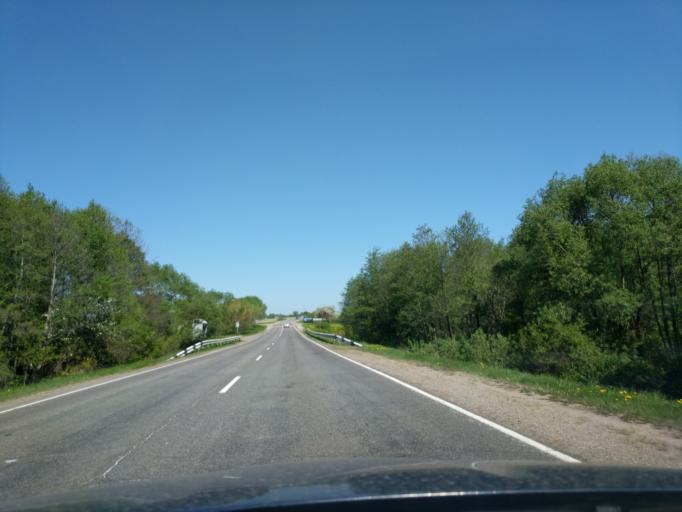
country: BY
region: Minsk
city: Il'ya
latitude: 54.2973
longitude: 27.4801
